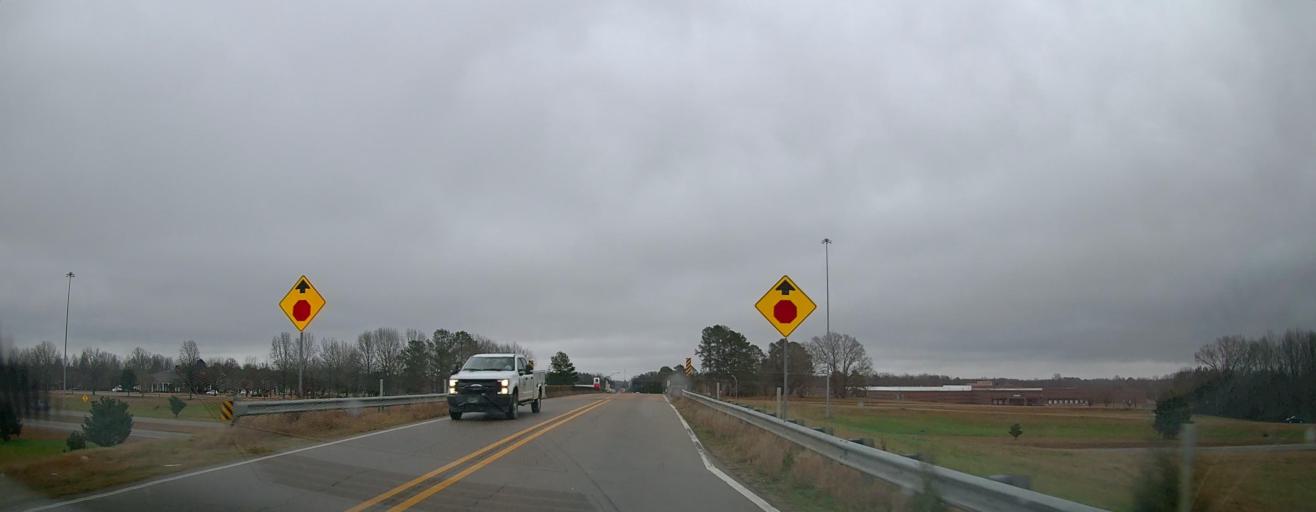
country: US
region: Mississippi
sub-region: Alcorn County
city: Corinth
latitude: 34.9091
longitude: -88.5452
